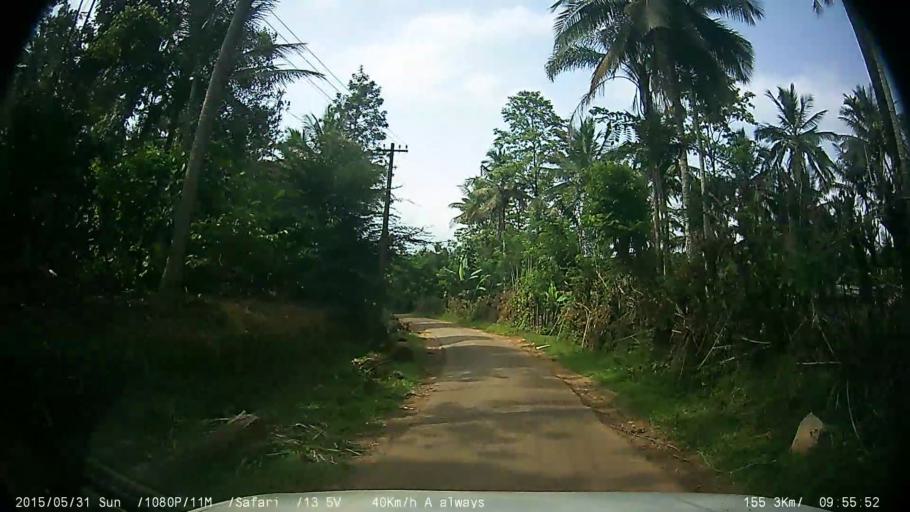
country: IN
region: Kerala
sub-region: Wayanad
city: Kalpetta
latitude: 11.6003
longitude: 76.0541
